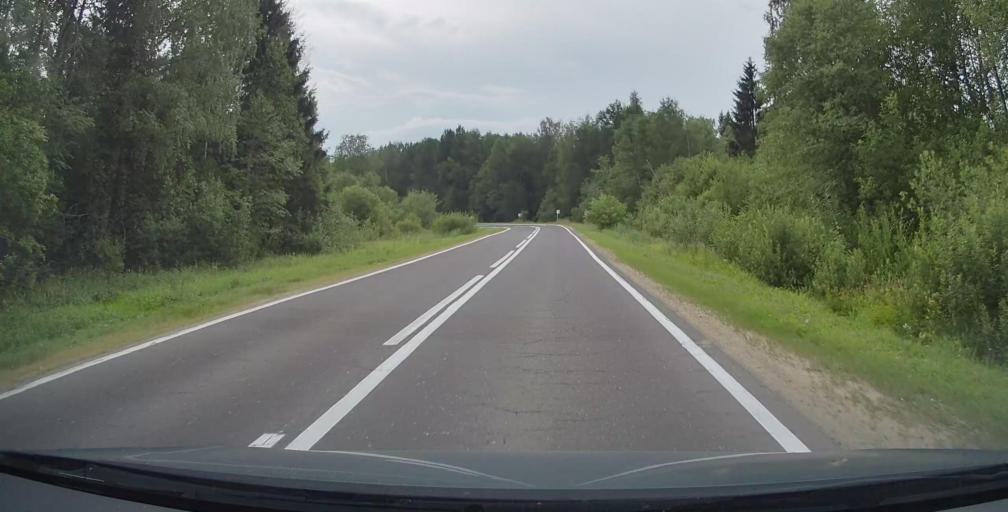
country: RU
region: Jaroslavl
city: Rybinsk
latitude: 57.9584
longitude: 38.7199
